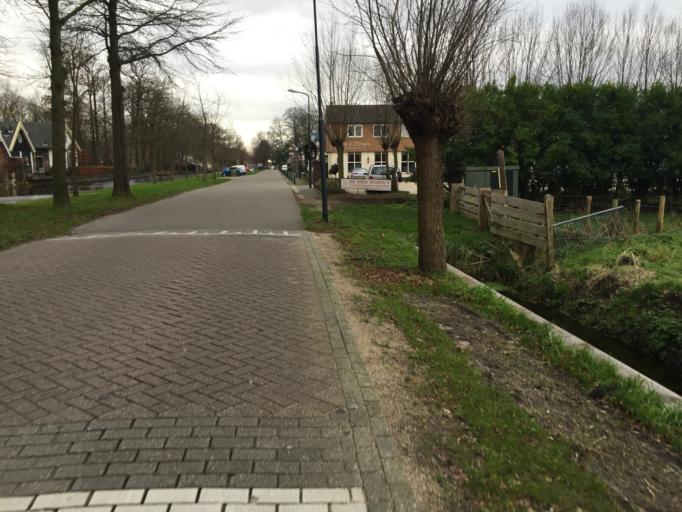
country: NL
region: North Holland
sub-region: Gemeente Wijdemeren
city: Kortenhoef
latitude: 52.2530
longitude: 5.1203
